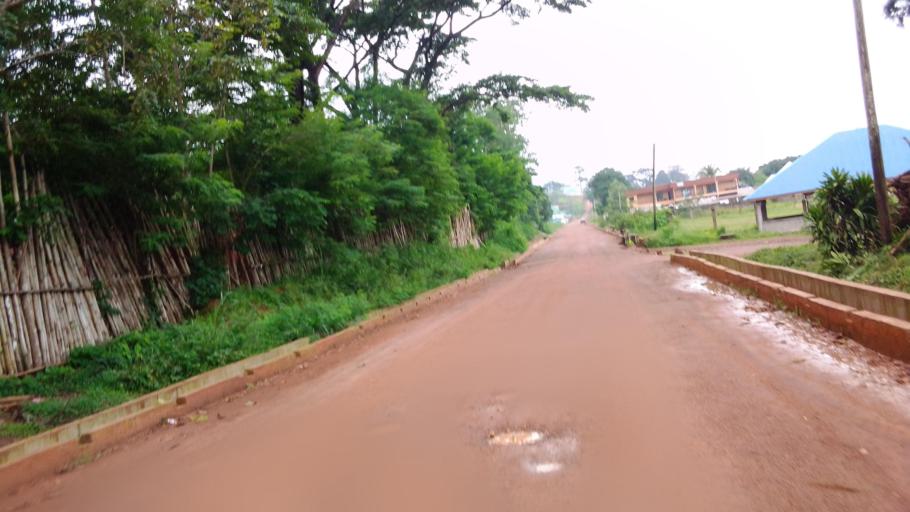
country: SL
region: Eastern Province
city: Kenema
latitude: 7.8881
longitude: -11.1918
